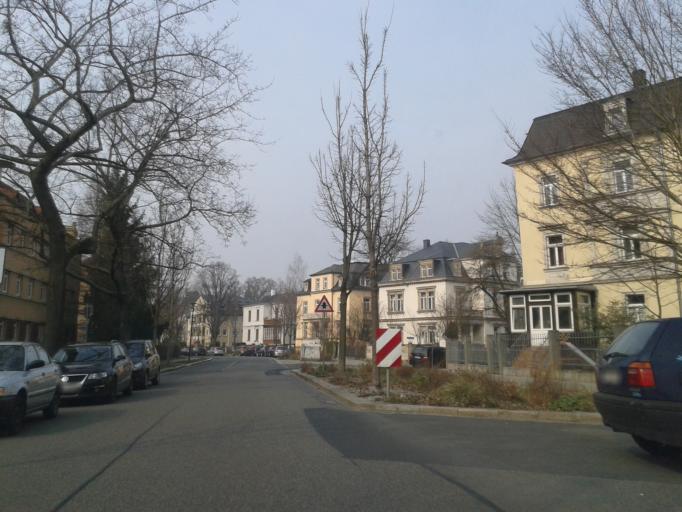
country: DE
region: Saxony
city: Dresden
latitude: 51.0215
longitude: 13.7683
